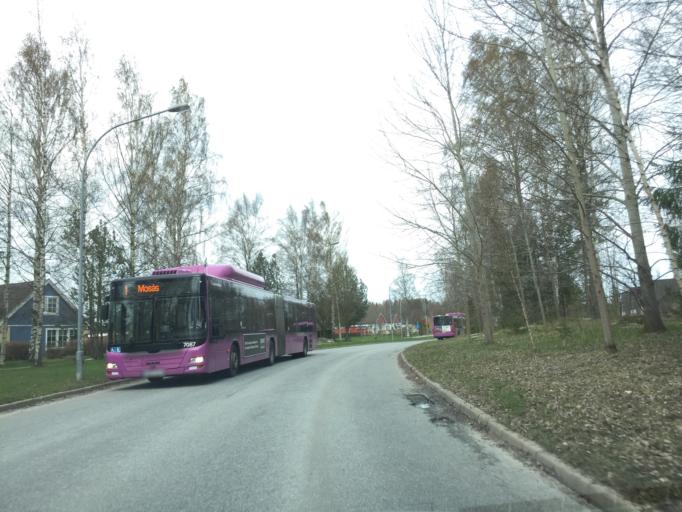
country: SE
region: OErebro
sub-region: Orebro Kommun
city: Orebro
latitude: 59.3114
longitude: 15.1834
